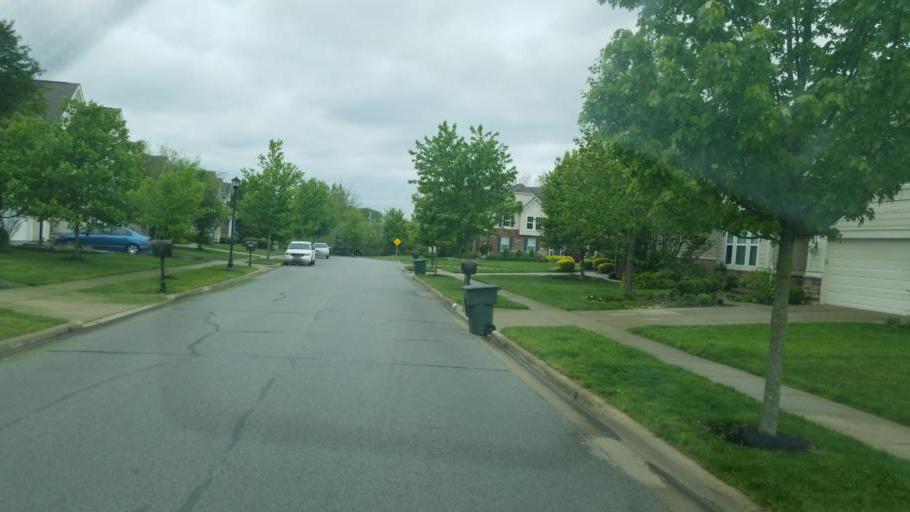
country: US
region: Ohio
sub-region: Franklin County
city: Worthington
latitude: 40.1187
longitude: -83.0427
